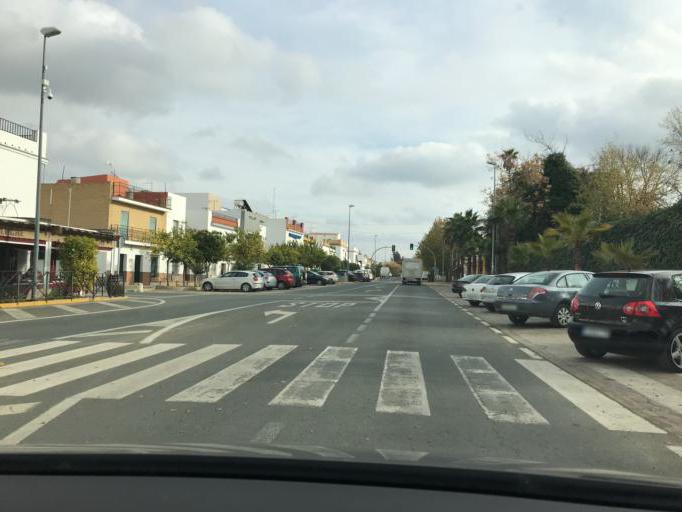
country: ES
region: Andalusia
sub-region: Provincia de Sevilla
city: La Campana
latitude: 37.5669
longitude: -5.4286
